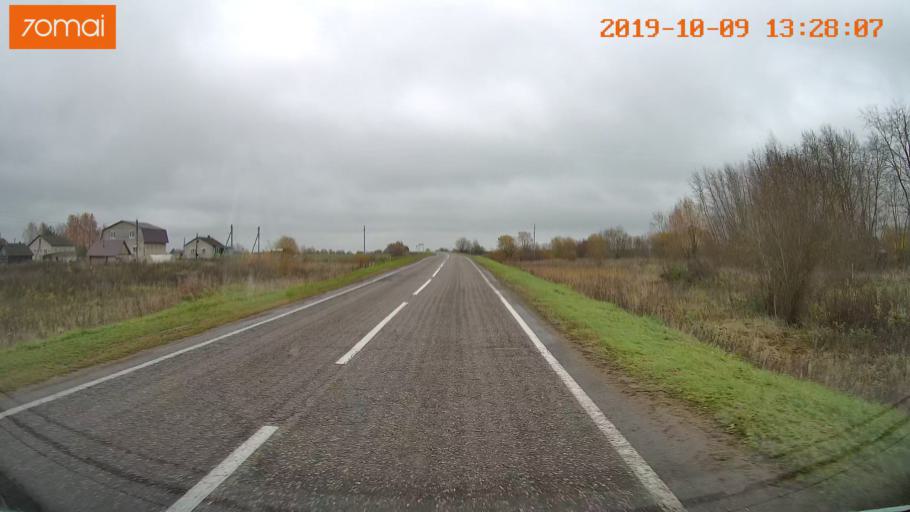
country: RU
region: Jaroslavl
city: Lyubim
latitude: 58.3147
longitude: 40.9608
